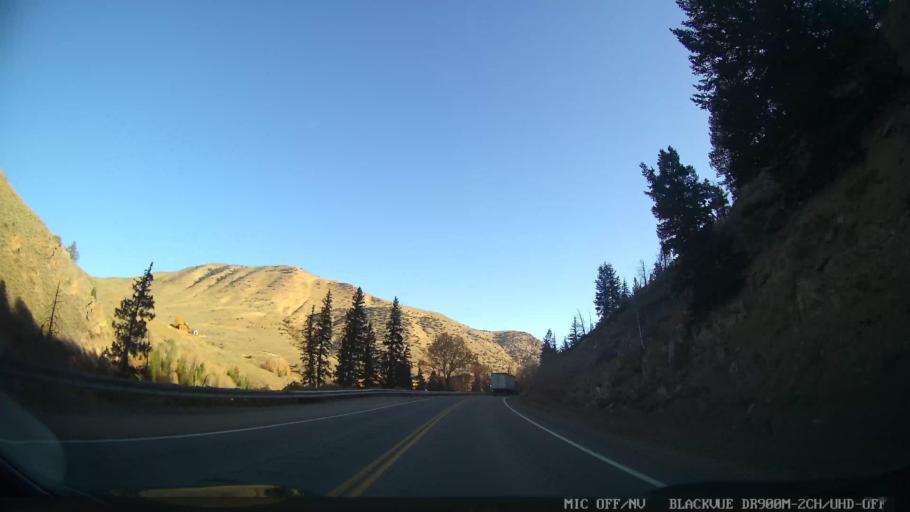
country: US
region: Colorado
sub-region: Grand County
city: Hot Sulphur Springs
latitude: 40.0690
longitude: -106.1129
